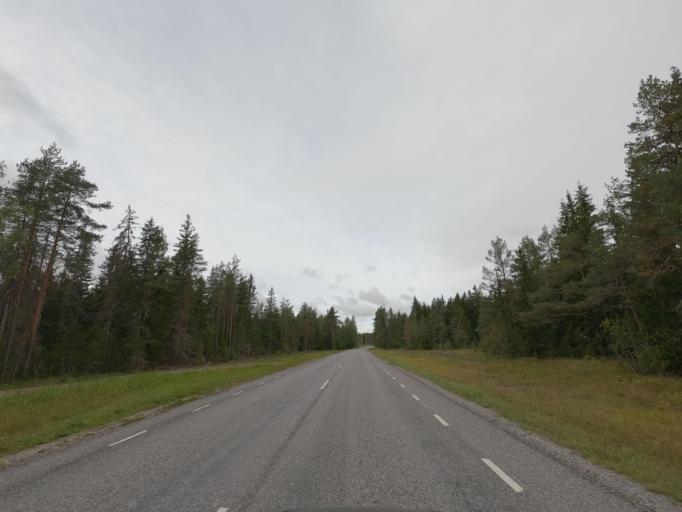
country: EE
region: Raplamaa
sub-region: Rapla vald
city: Rapla
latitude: 59.0053
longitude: 24.6238
